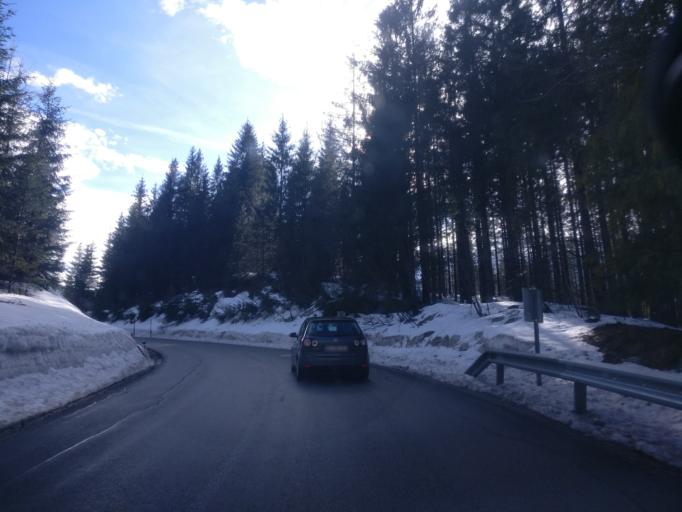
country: AT
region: Styria
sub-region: Politischer Bezirk Liezen
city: Sankt Gallen
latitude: 47.6365
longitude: 14.5628
